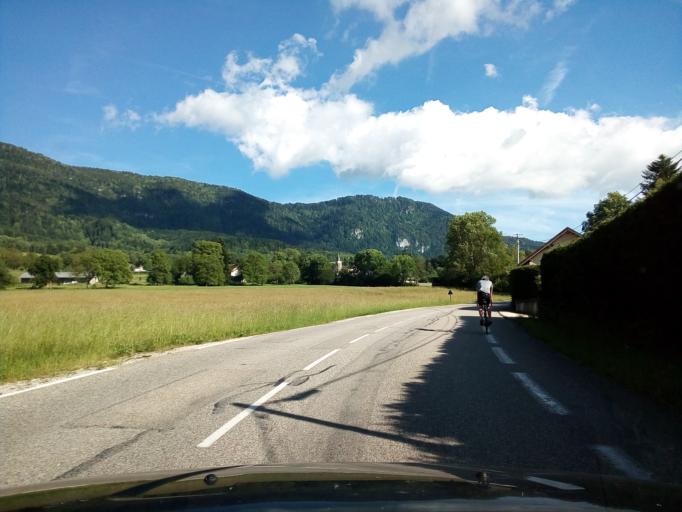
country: FR
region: Rhone-Alpes
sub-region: Departement de la Savoie
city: La Bridoire
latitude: 45.5126
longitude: 5.7706
